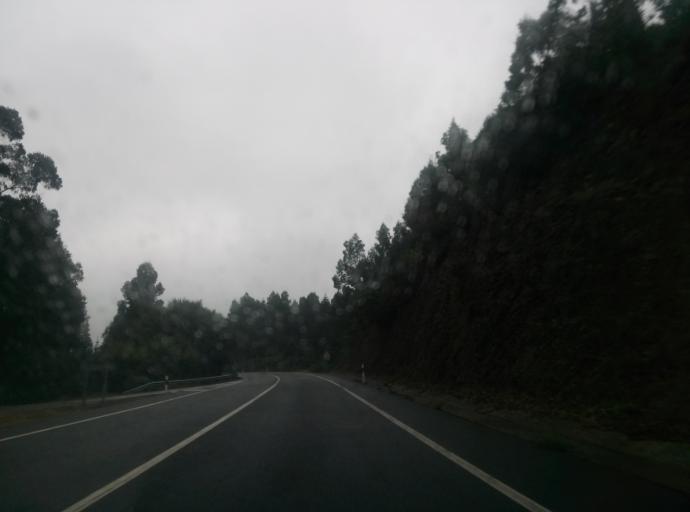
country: ES
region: Galicia
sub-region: Provincia de Lugo
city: Muras
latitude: 43.5514
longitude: -7.6501
